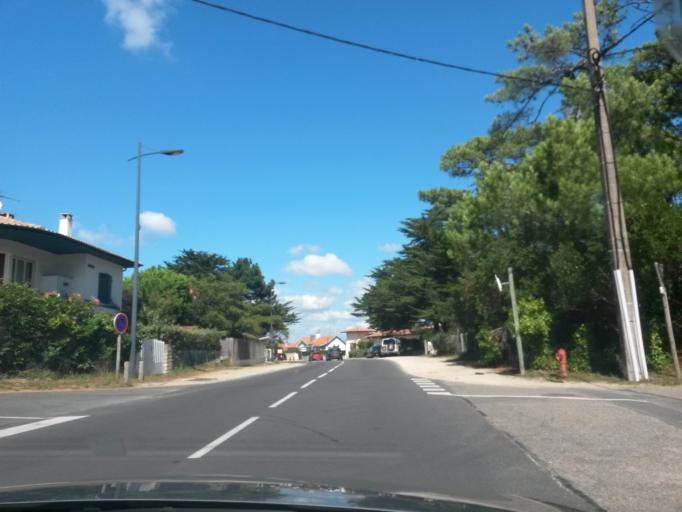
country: FR
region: Aquitaine
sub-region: Departement de la Gironde
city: Arcachon
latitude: 44.6975
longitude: -1.2309
